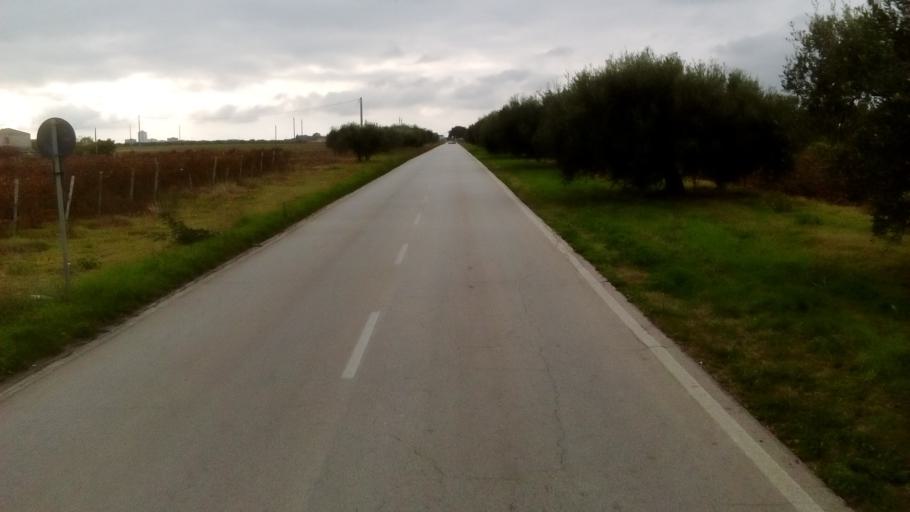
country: IT
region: Abruzzo
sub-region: Provincia di Chieti
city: Vasto
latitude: 42.1550
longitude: 14.7006
